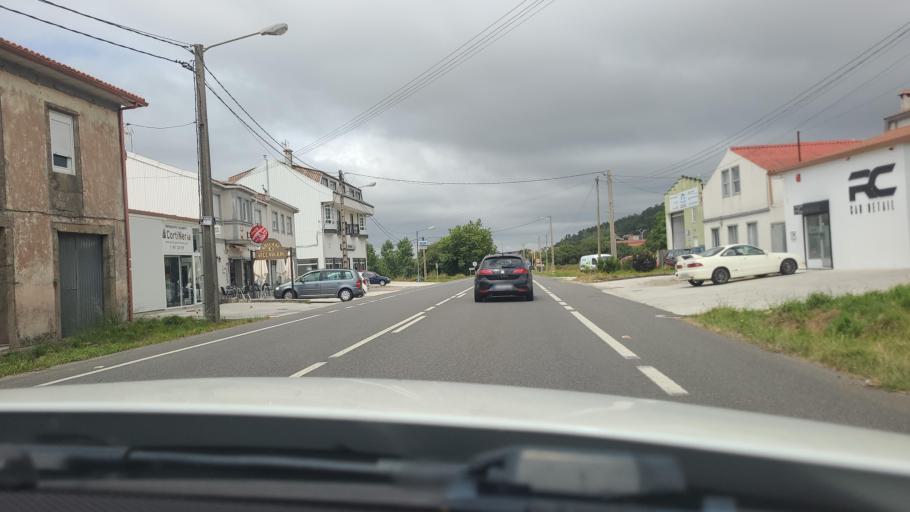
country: ES
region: Galicia
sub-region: Provincia da Coruna
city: Cee
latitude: 42.9827
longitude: -9.1864
